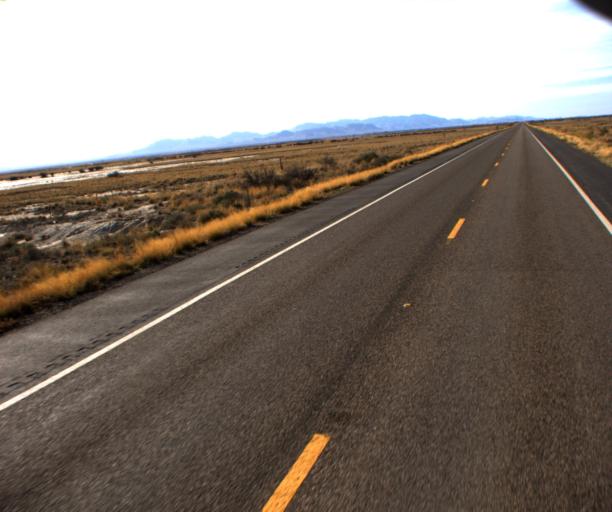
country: US
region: Arizona
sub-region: Cochise County
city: Willcox
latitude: 32.2043
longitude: -109.7706
